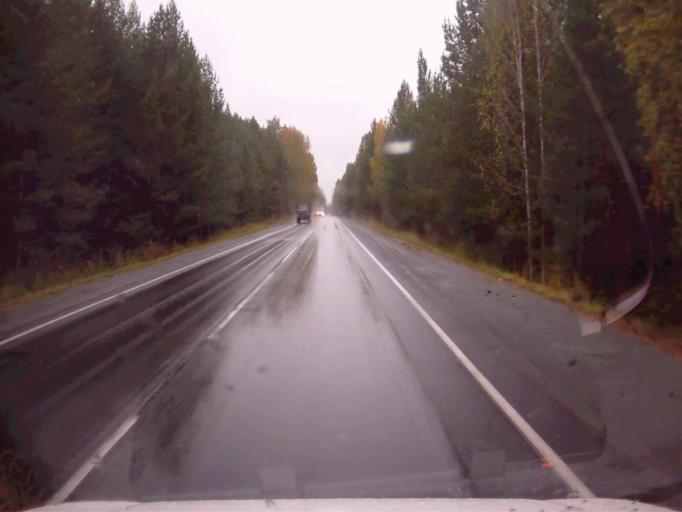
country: RU
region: Chelyabinsk
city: Tayginka
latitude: 55.5824
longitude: 60.6387
